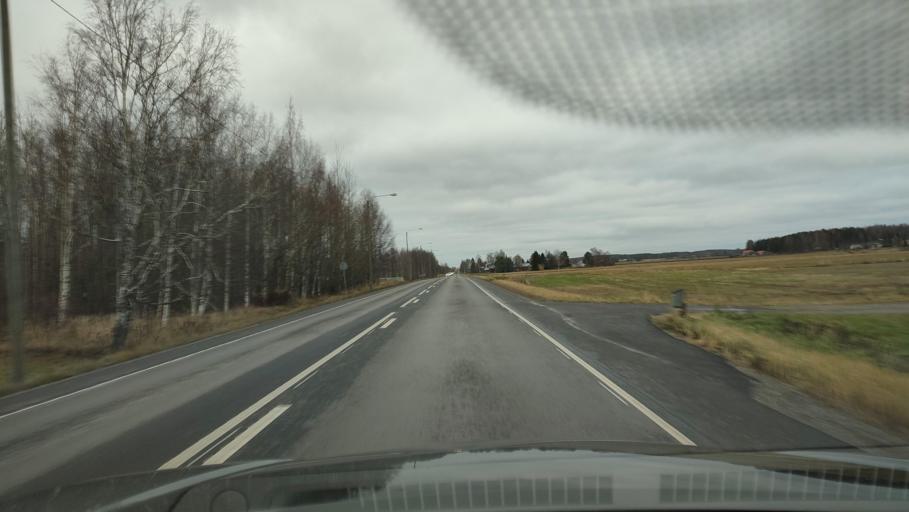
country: FI
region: Southern Ostrobothnia
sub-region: Seinaejoki
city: Ilmajoki
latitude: 62.6953
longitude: 22.5032
